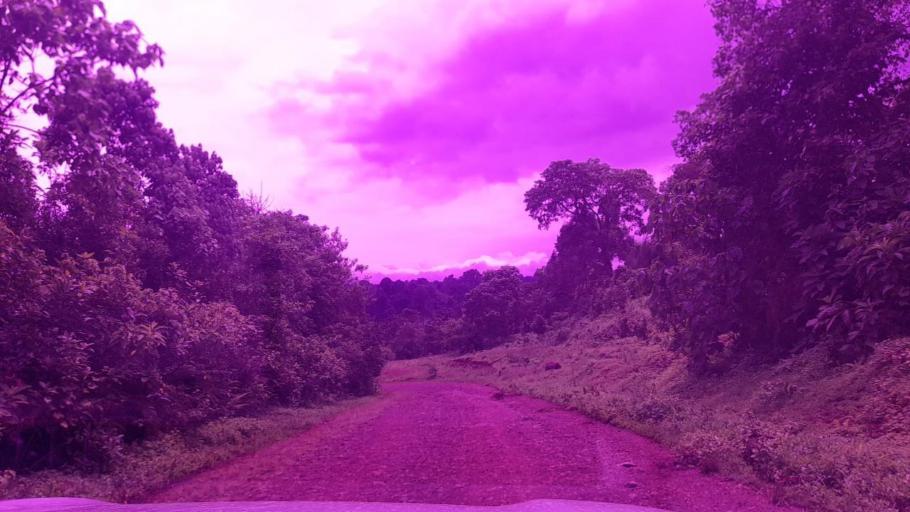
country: ET
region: Southern Nations, Nationalities, and People's Region
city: Tippi
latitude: 7.6330
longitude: 35.5691
